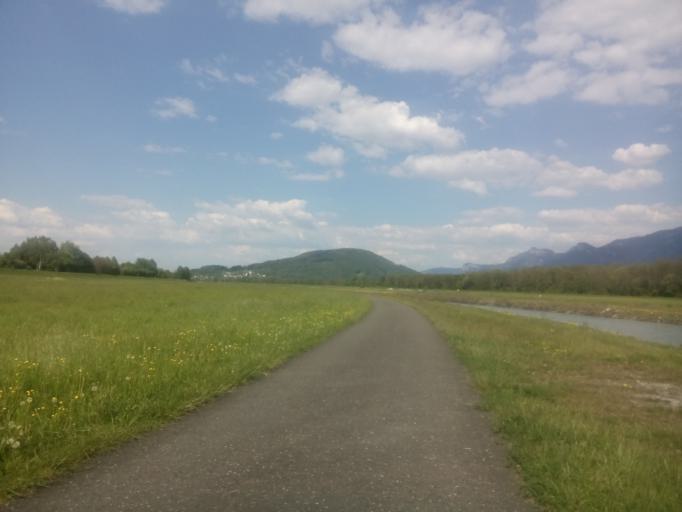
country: AT
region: Vorarlberg
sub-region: Politischer Bezirk Feldkirch
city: Meiningen
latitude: 47.3115
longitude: 9.5810
